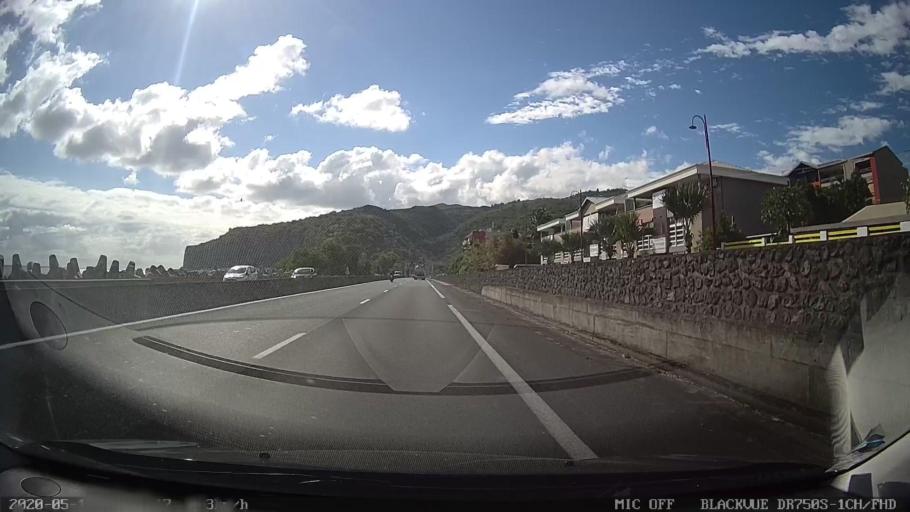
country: RE
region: Reunion
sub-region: Reunion
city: La Possession
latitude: -20.9240
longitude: 55.3391
